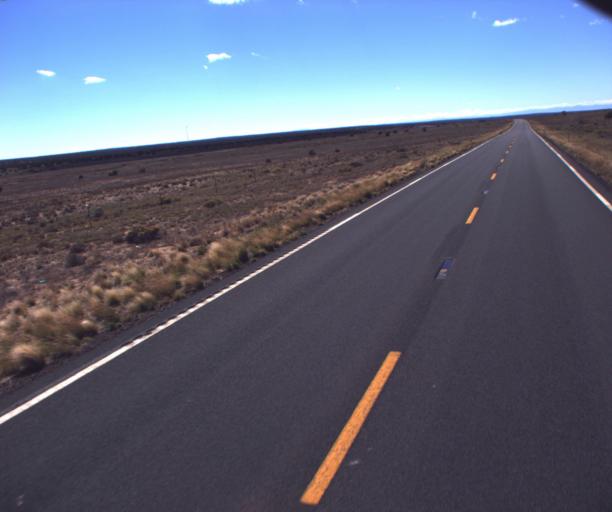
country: US
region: Arizona
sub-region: Apache County
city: Houck
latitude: 34.9379
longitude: -109.2354
